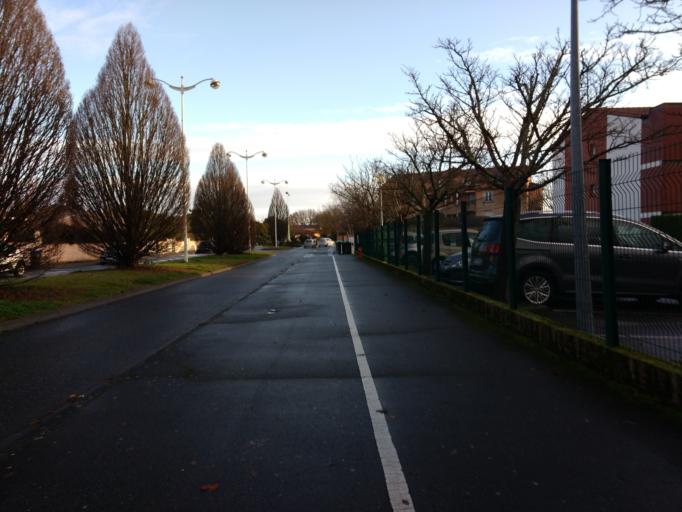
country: FR
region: Midi-Pyrenees
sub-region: Departement de la Haute-Garonne
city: Tournefeuille
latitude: 43.5897
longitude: 1.3401
